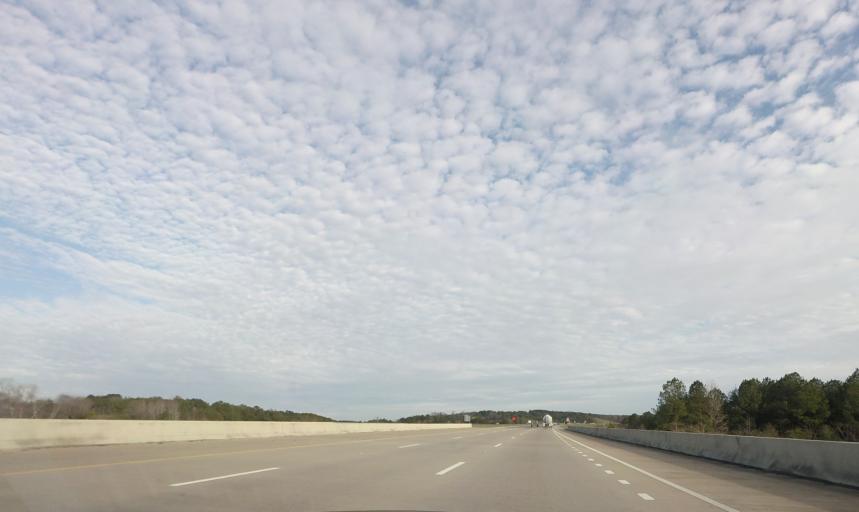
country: US
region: Alabama
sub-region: Jefferson County
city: Graysville
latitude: 33.6643
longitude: -87.0319
